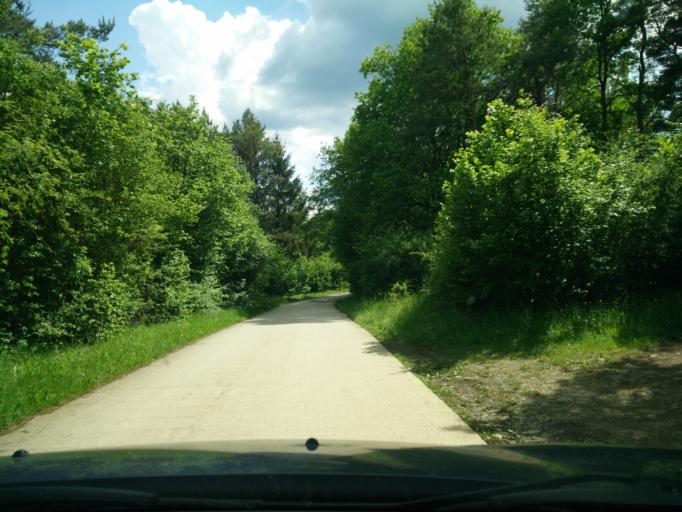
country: FR
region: Champagne-Ardenne
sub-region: Departement des Ardennes
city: Vireux-Molhain
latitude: 50.0832
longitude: 4.6183
